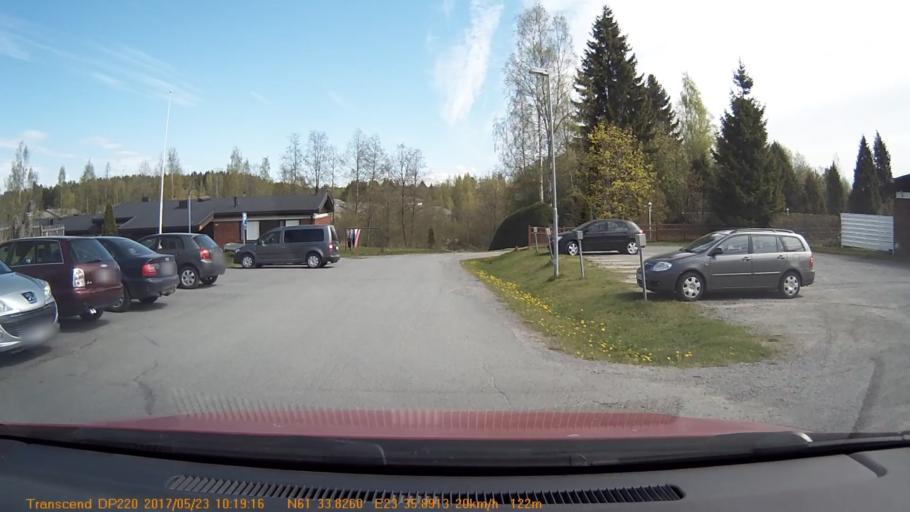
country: FI
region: Pirkanmaa
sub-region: Tampere
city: Yloejaervi
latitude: 61.5638
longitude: 23.5980
